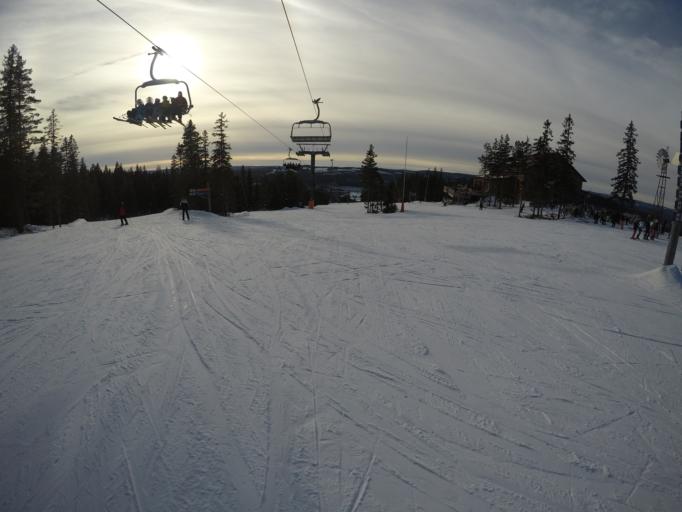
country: SE
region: Dalarna
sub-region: Borlange Kommun
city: Borlaenge
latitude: 60.3818
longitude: 15.4225
